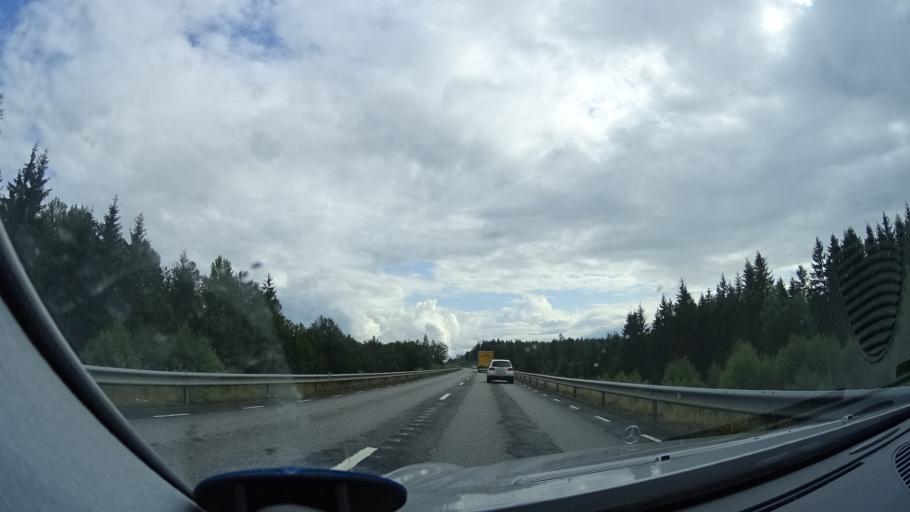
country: SE
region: Blekinge
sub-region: Karlshamns Kommun
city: Svangsta
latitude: 56.3114
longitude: 14.8838
